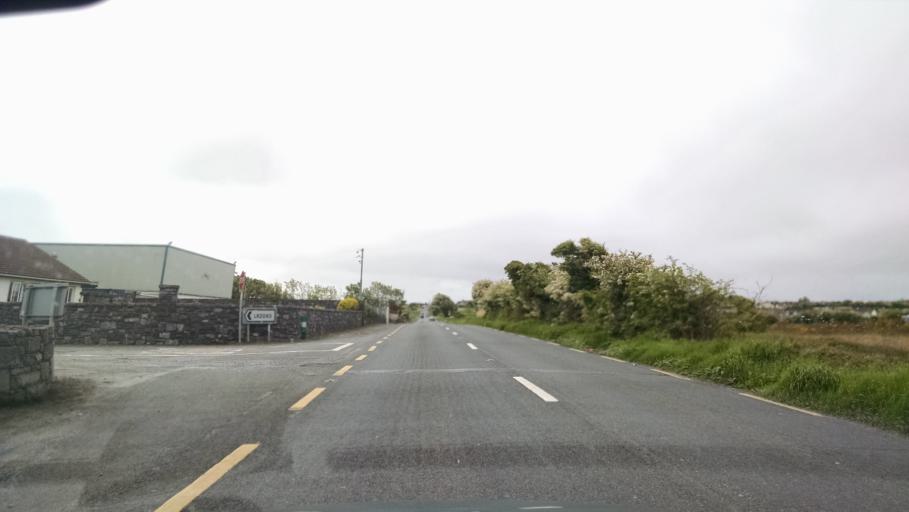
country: IE
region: Connaught
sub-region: County Galway
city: Gaillimh
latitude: 53.3209
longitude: -9.0217
